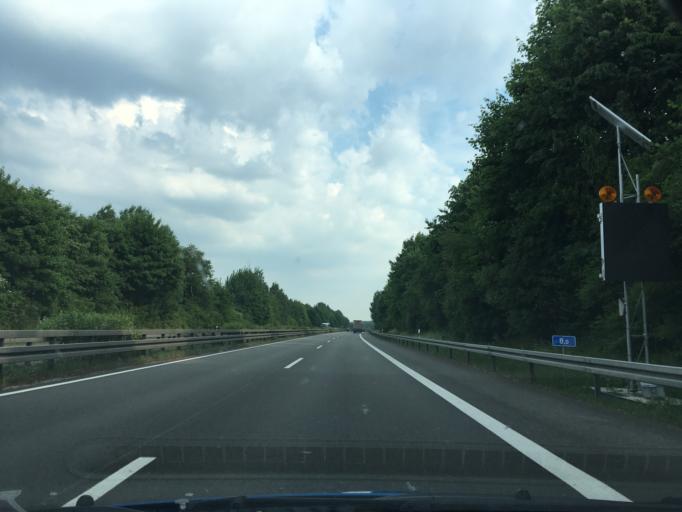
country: DE
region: Lower Saxony
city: Stelle
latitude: 53.3681
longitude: 10.1053
